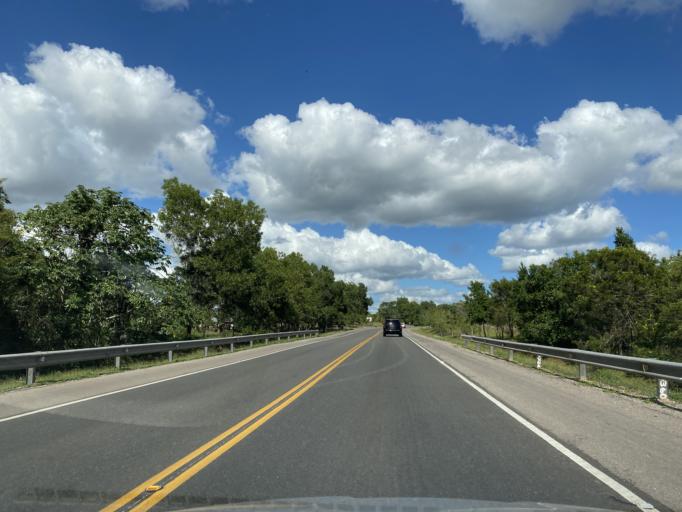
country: DO
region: Monte Plata
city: Monte Plata
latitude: 18.7574
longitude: -69.7645
